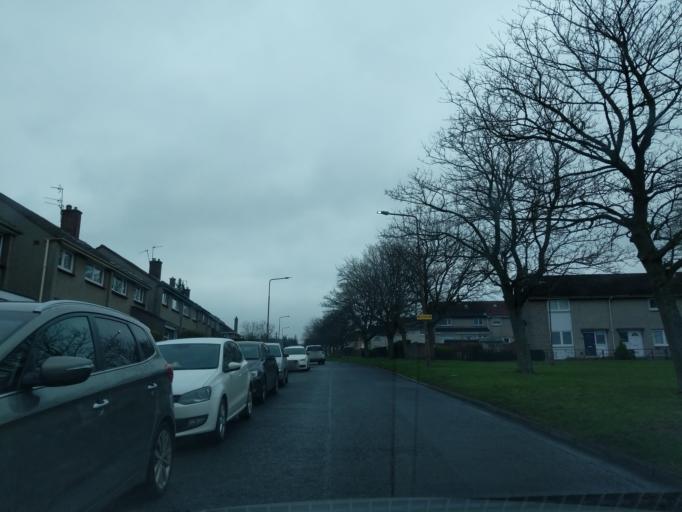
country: GB
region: Scotland
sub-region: Edinburgh
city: Currie
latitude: 55.8990
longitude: -3.3151
